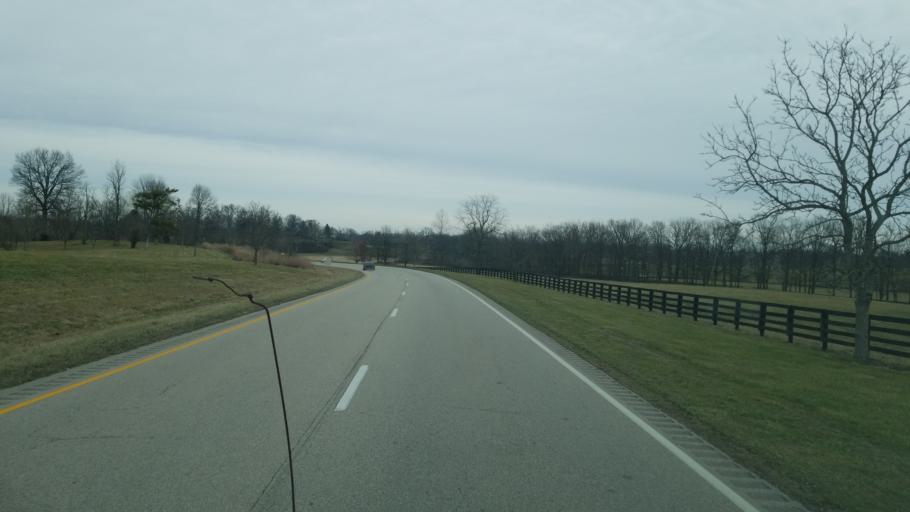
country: US
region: Kentucky
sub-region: Bourbon County
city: Paris
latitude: 38.1675
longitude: -84.3141
